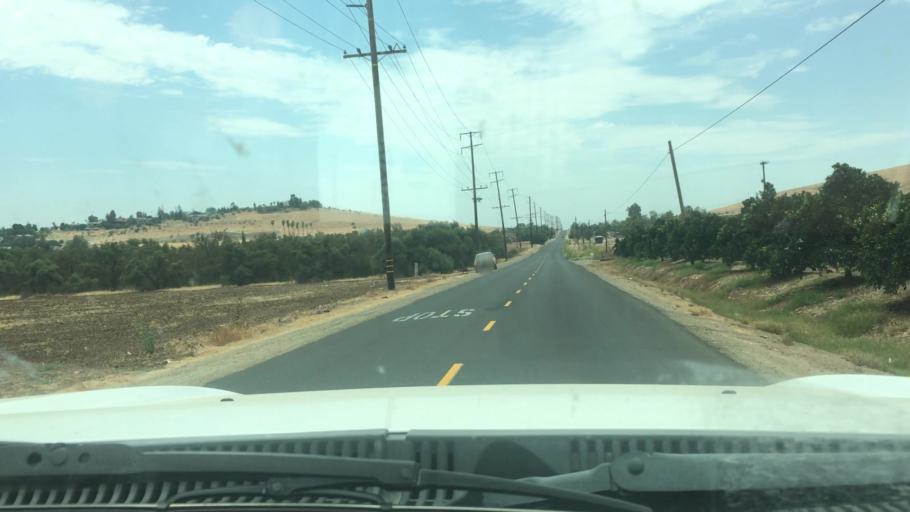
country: US
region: California
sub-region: Tulare County
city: Porterville
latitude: 36.0965
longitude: -119.0109
